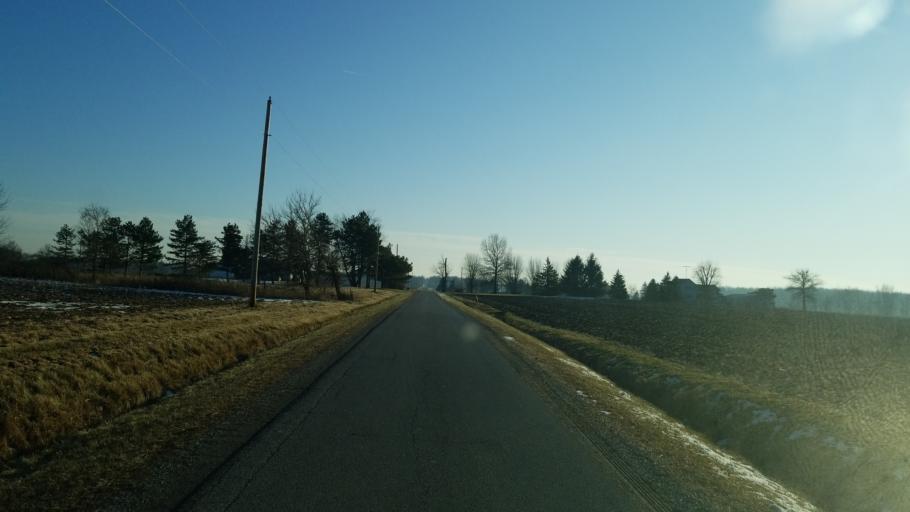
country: US
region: Ohio
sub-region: Crawford County
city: Bucyrus
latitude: 40.9481
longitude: -82.9209
